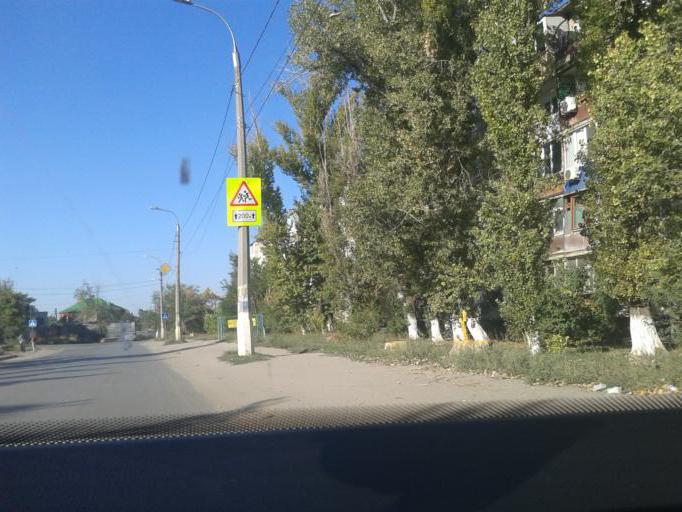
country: RU
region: Volgograd
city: Gorodishche
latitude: 48.7702
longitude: 44.4973
